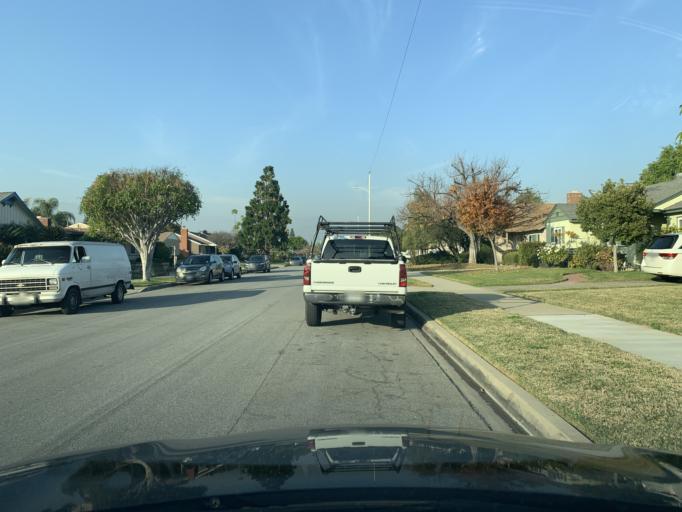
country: US
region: California
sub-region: Los Angeles County
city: Covina
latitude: 34.0936
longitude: -117.8929
